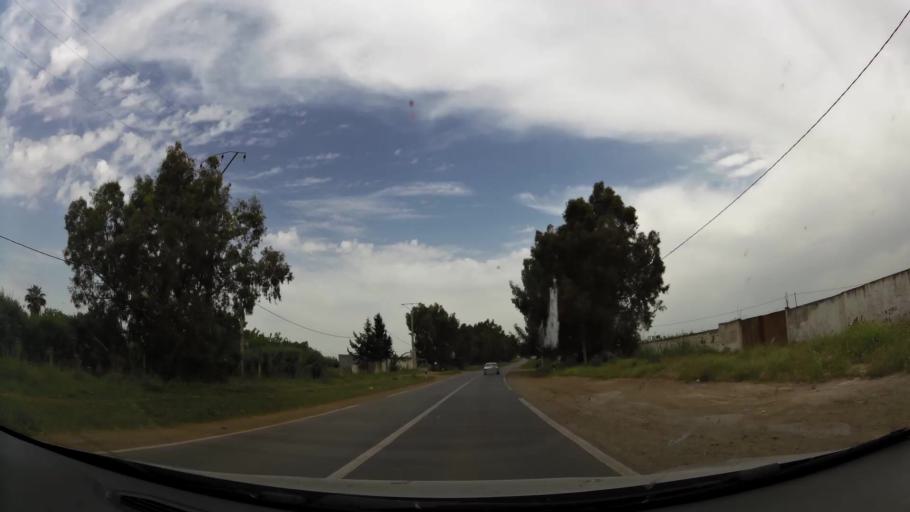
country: MA
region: Rabat-Sale-Zemmour-Zaer
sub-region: Khemisset
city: Tiflet
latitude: 33.8705
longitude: -6.2769
